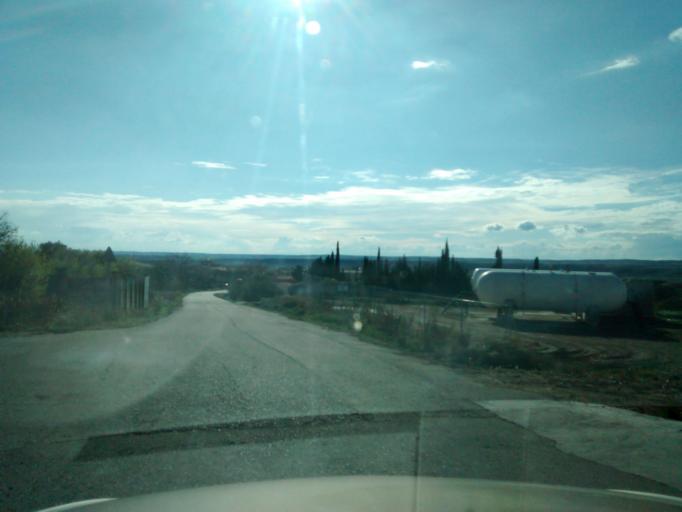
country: ES
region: Aragon
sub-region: Provincia de Zaragoza
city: San Mateo de Gallego
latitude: 41.8338
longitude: -0.7595
